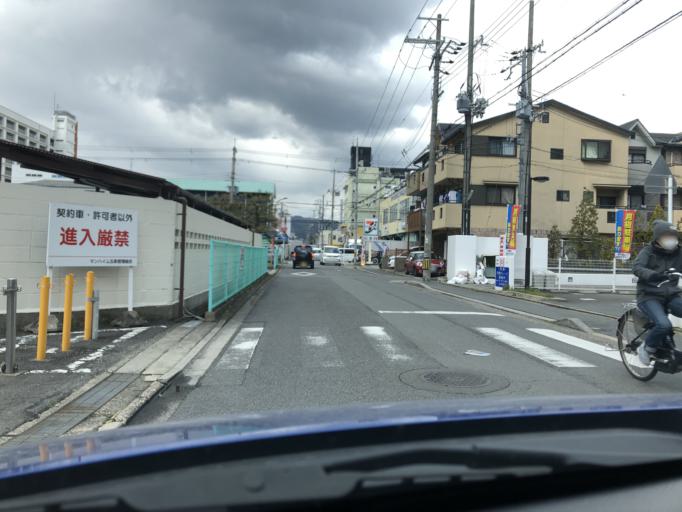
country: JP
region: Kyoto
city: Muko
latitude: 34.9975
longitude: 135.7220
